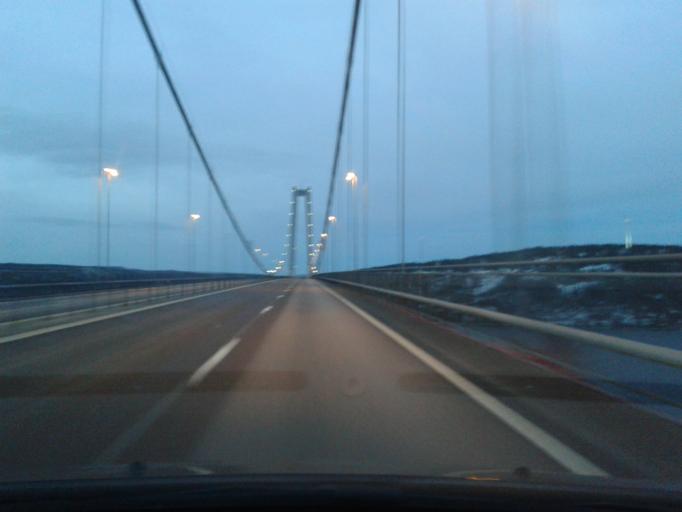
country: SE
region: Vaesternorrland
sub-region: Haernoesands Kommun
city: Haernoesand
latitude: 62.7957
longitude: 17.9349
